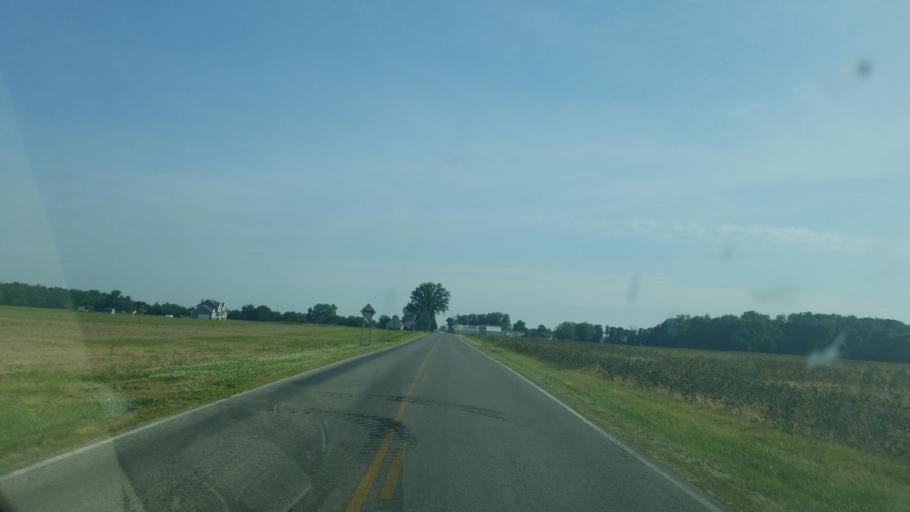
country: US
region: Ohio
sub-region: Hancock County
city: Arlington
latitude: 40.8935
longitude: -83.6986
